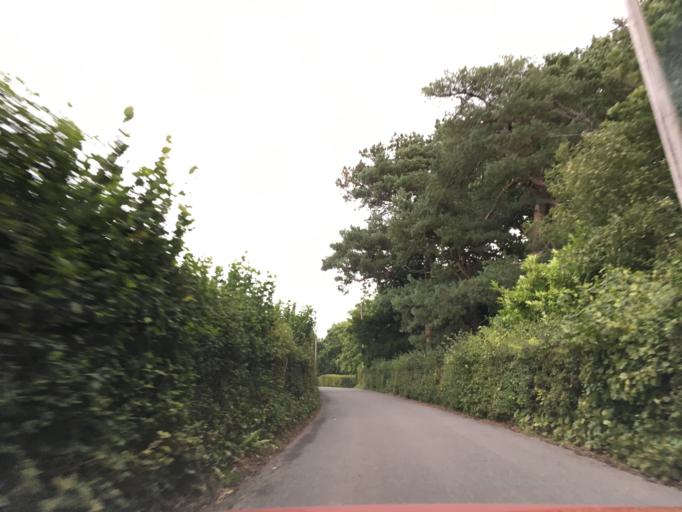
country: GB
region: Wales
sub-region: Newport
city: Caerleon
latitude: 51.6247
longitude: -2.9395
